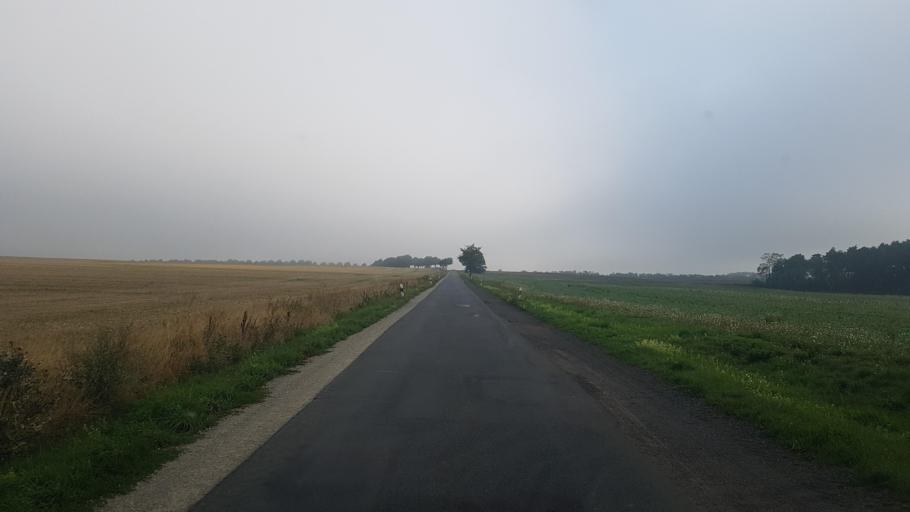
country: DE
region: Brandenburg
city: Niemegk
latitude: 52.0083
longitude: 12.6838
